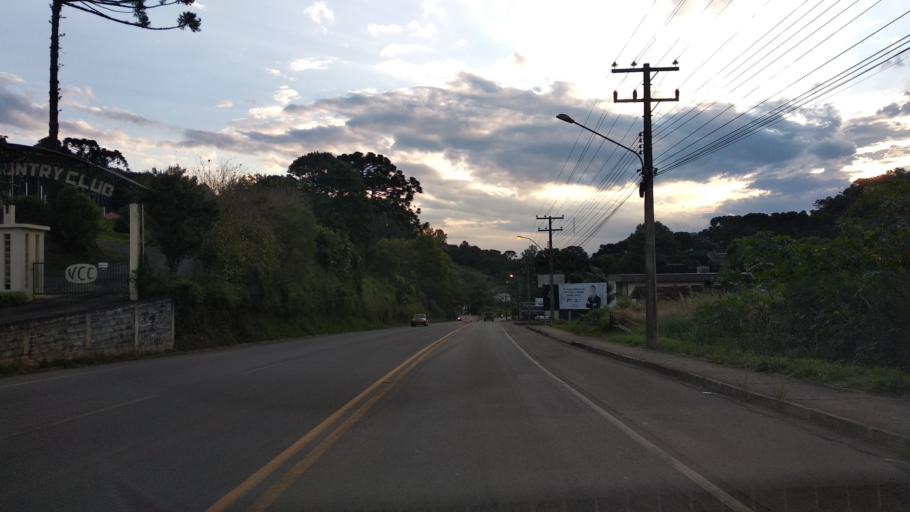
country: BR
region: Santa Catarina
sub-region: Videira
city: Videira
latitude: -27.0024
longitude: -51.1286
